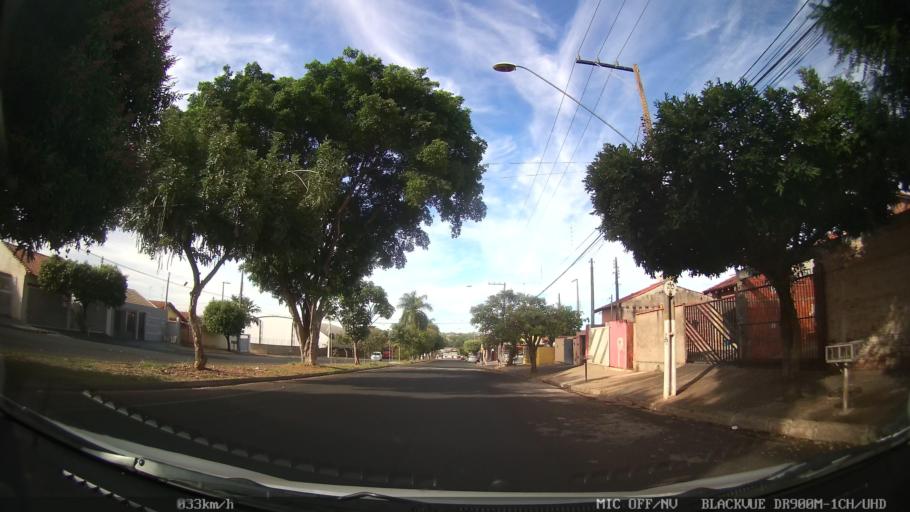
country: BR
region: Sao Paulo
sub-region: Catanduva
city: Catanduva
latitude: -21.1311
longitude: -48.9956
